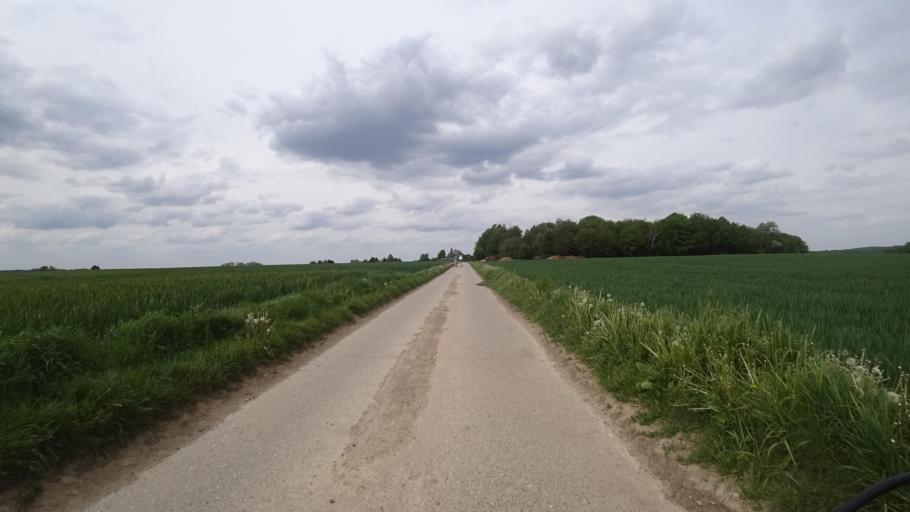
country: BE
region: Wallonia
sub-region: Province du Brabant Wallon
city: Chaumont-Gistoux
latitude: 50.6857
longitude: 4.6700
